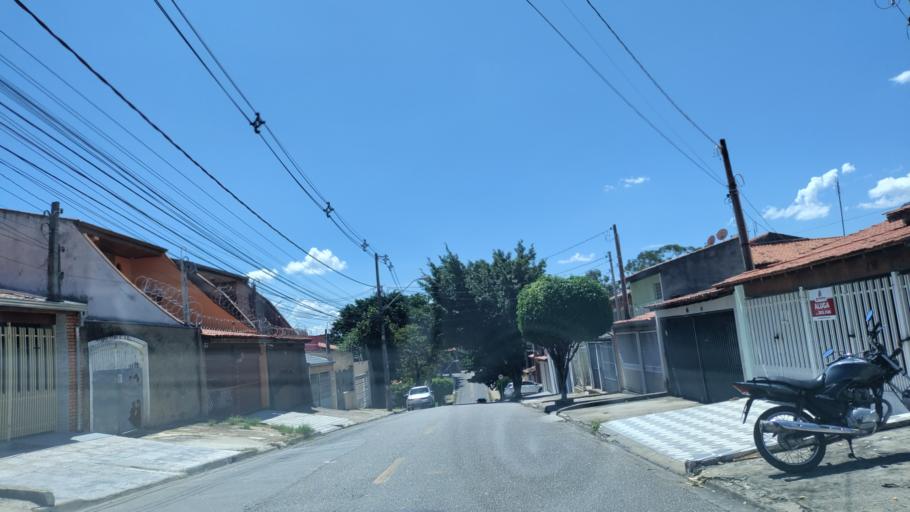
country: BR
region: Sao Paulo
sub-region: Sorocaba
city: Sorocaba
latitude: -23.4599
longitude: -47.4750
